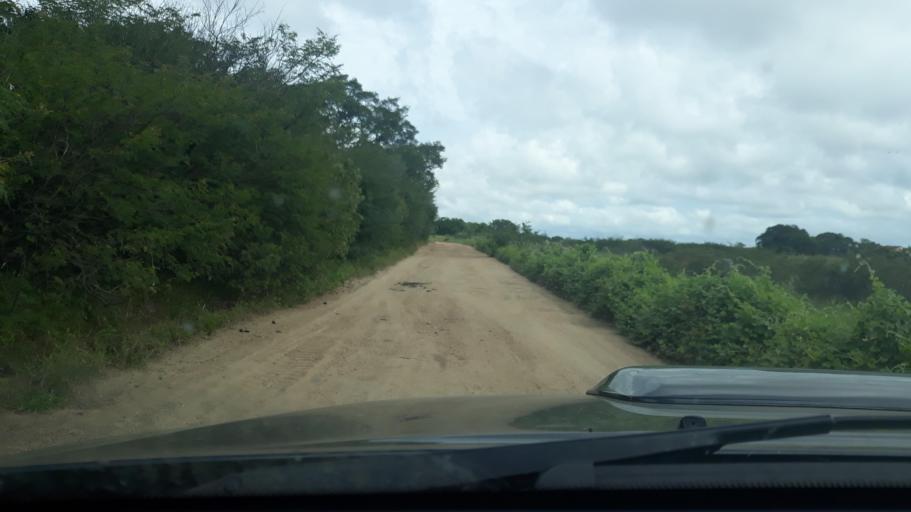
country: BR
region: Bahia
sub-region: Riacho De Santana
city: Riacho de Santana
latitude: -13.9114
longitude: -42.9492
